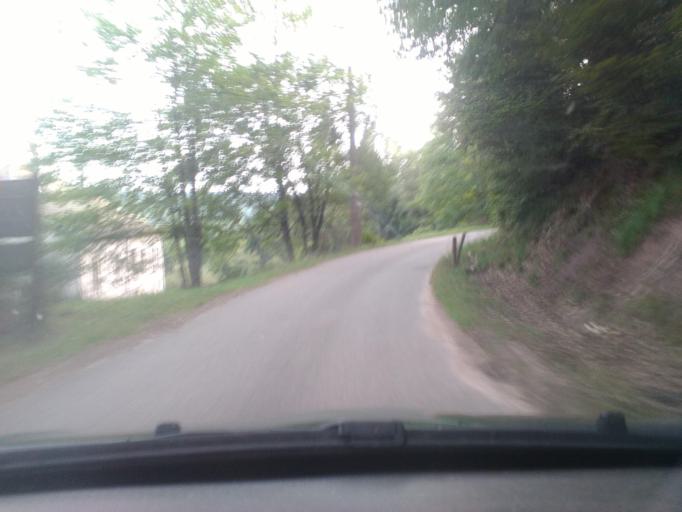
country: FR
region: Lorraine
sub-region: Departement des Vosges
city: Corcieux
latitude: 48.2051
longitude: 6.8806
